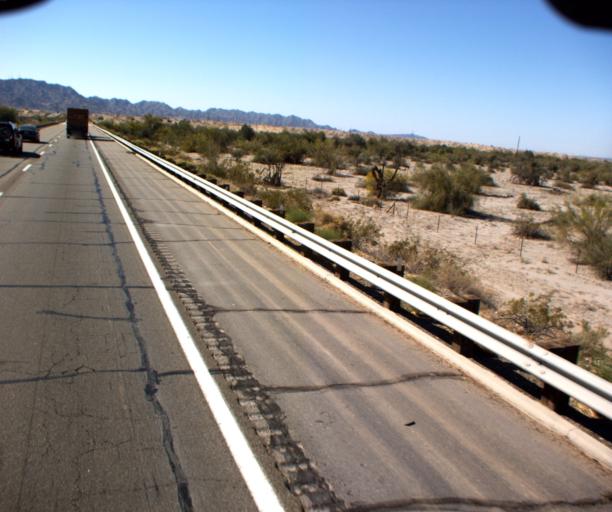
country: US
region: Arizona
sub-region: Yuma County
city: Wellton
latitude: 32.6589
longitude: -114.2498
